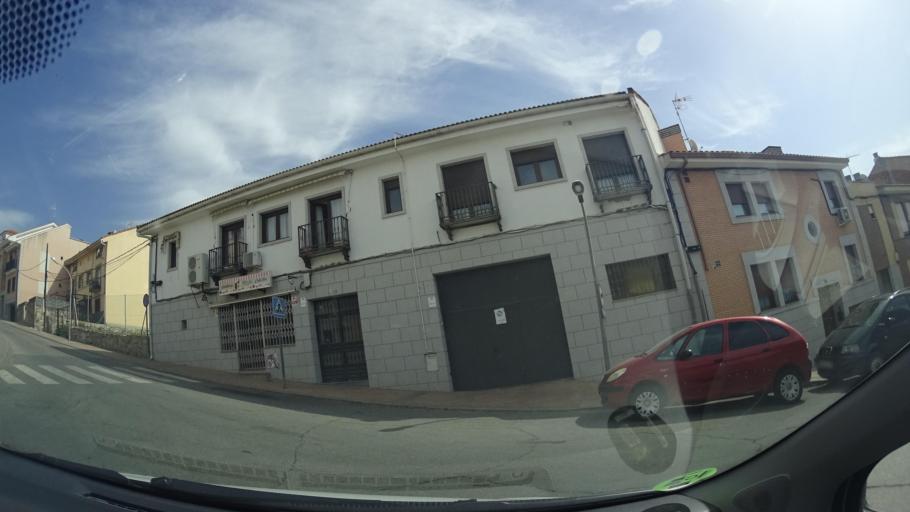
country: ES
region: Madrid
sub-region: Provincia de Madrid
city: Colmenar Viejo
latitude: 40.6558
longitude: -3.7659
